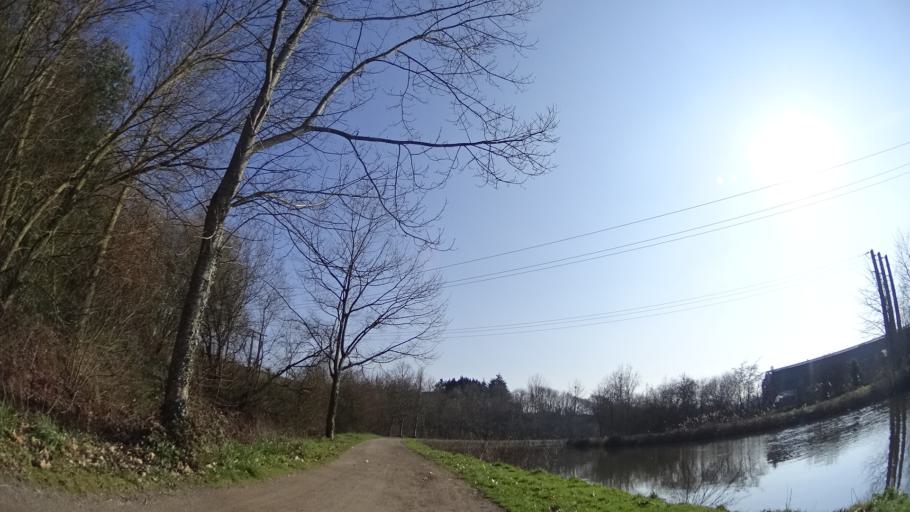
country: FR
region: Brittany
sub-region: Departement d'Ille-et-Vilaine
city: Saint-Gregoire
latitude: 48.1409
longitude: -1.6741
